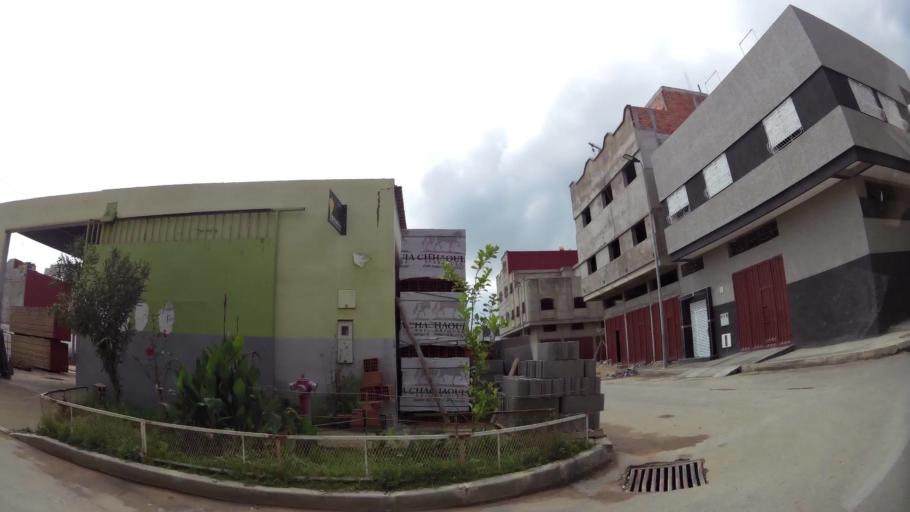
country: MA
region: Rabat-Sale-Zemmour-Zaer
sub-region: Khemisset
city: Tiflet
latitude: 33.8896
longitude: -6.3284
